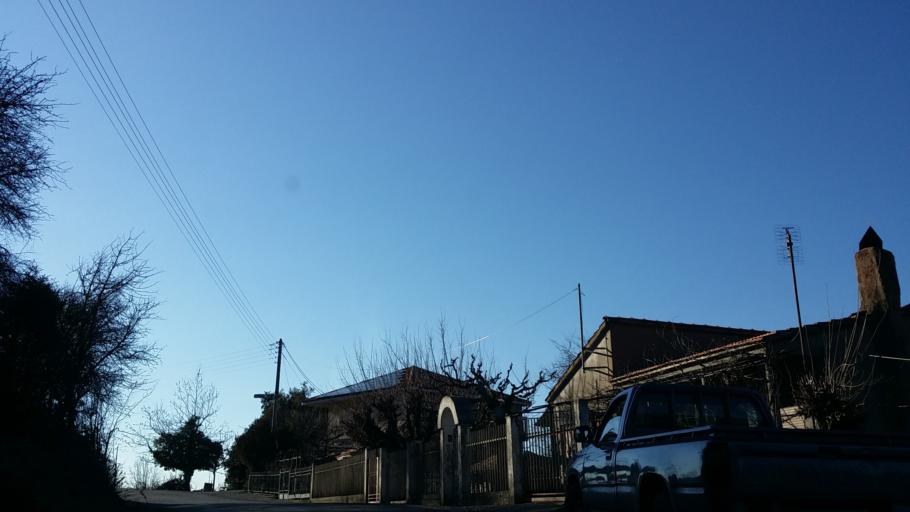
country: GR
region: Central Greece
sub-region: Nomos Evrytanias
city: Kerasochori
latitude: 38.8280
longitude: 21.5211
